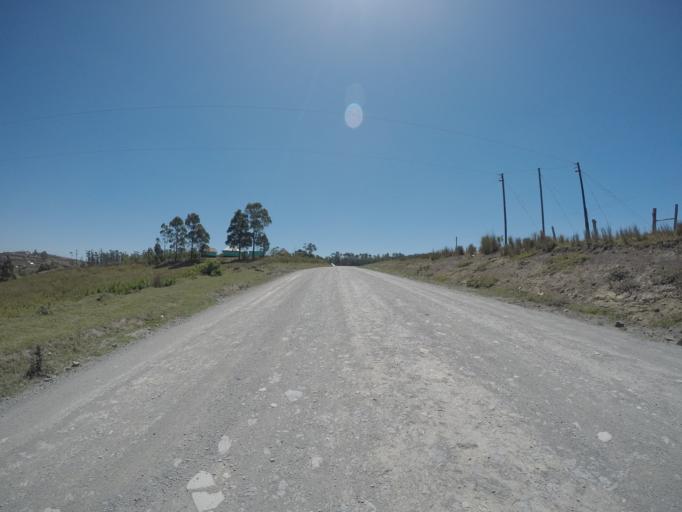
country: ZA
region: Eastern Cape
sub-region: OR Tambo District Municipality
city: Libode
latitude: -31.9646
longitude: 29.0251
